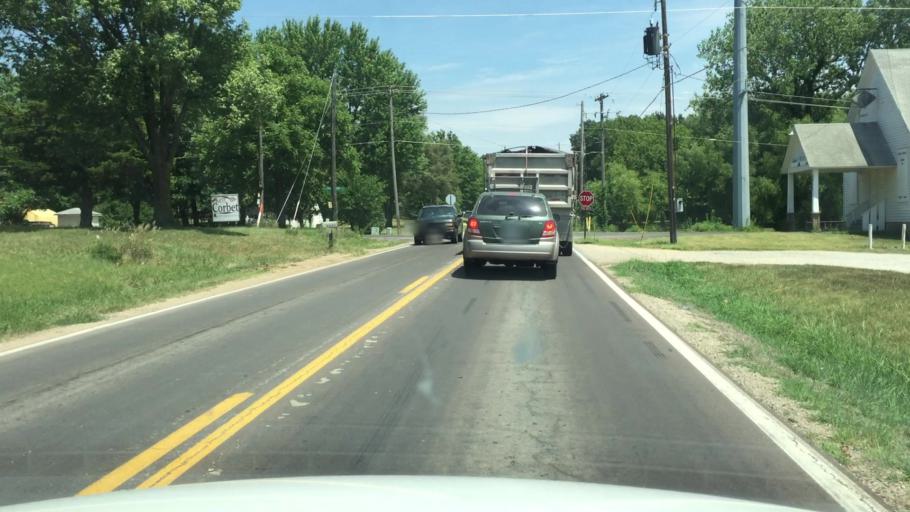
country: US
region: Kansas
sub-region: Shawnee County
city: Topeka
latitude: 38.9861
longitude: -95.5573
